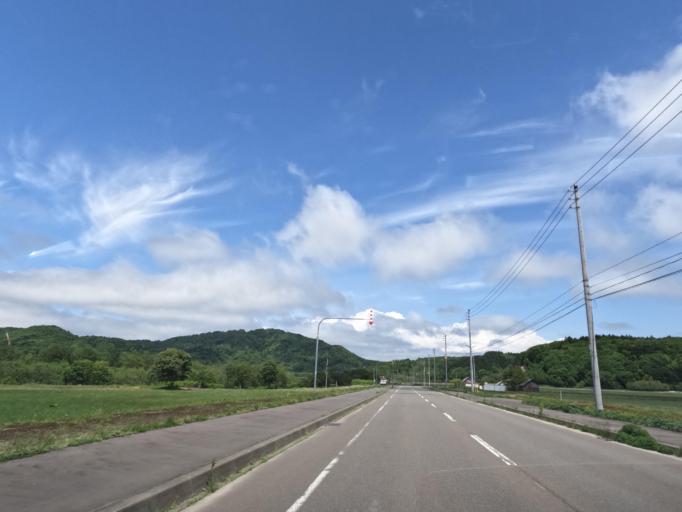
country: JP
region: Hokkaido
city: Tobetsu
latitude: 43.3050
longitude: 141.5529
